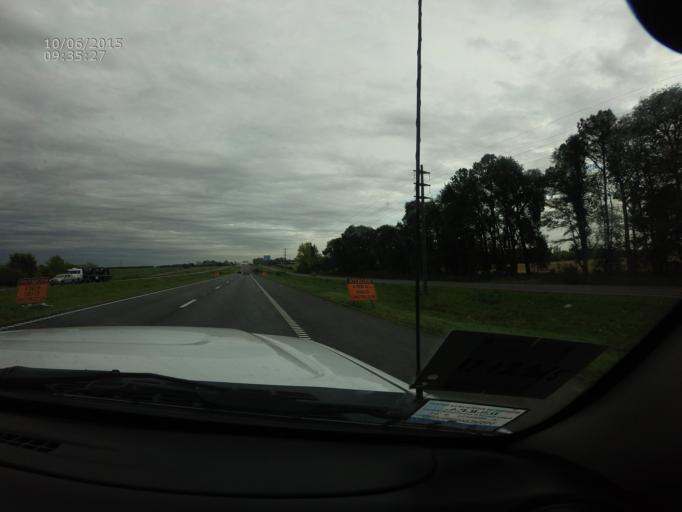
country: AR
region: Buenos Aires
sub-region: Partido de Zarate
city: Zarate
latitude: -34.1060
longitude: -59.1360
